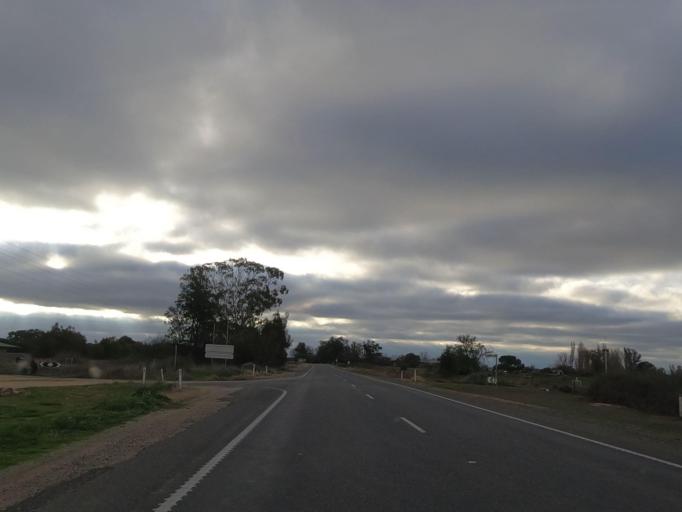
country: AU
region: Victoria
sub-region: Swan Hill
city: Swan Hill
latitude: -35.7268
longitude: 143.8911
